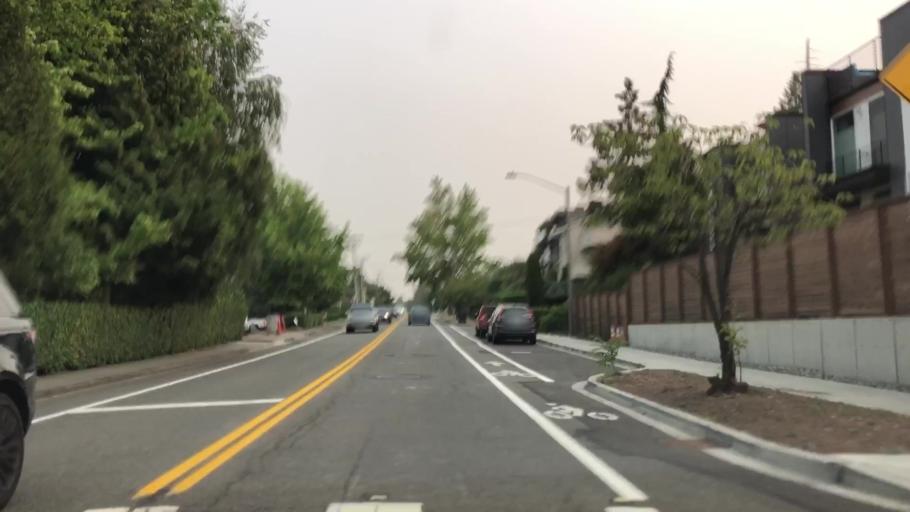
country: US
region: Washington
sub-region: King County
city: Kirkland
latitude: 47.6623
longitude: -122.2048
